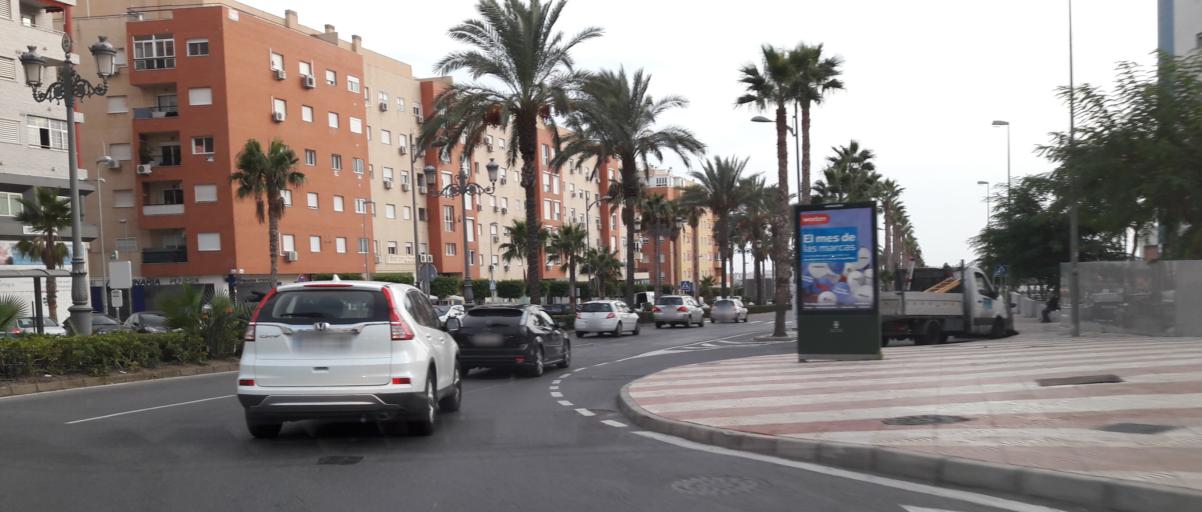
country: ES
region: Andalusia
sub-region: Provincia de Almeria
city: Aguadulce
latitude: 36.8033
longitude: -2.6001
